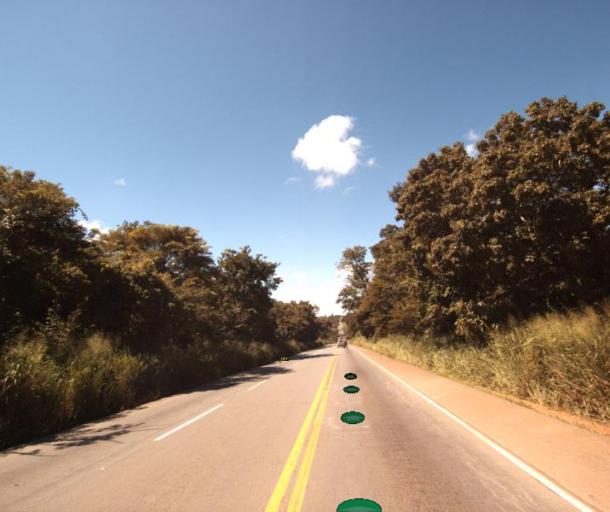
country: BR
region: Goias
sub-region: Jaragua
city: Jaragua
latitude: -15.6433
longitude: -49.3701
